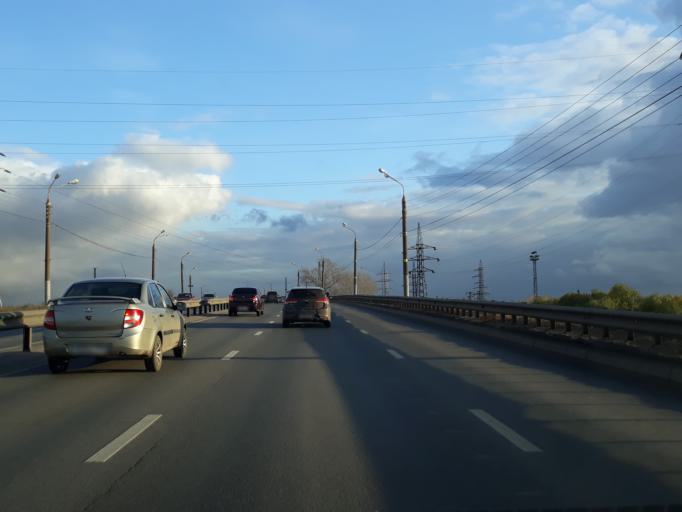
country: RU
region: Nizjnij Novgorod
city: Nizhniy Novgorod
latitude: 56.3081
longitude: 43.9024
